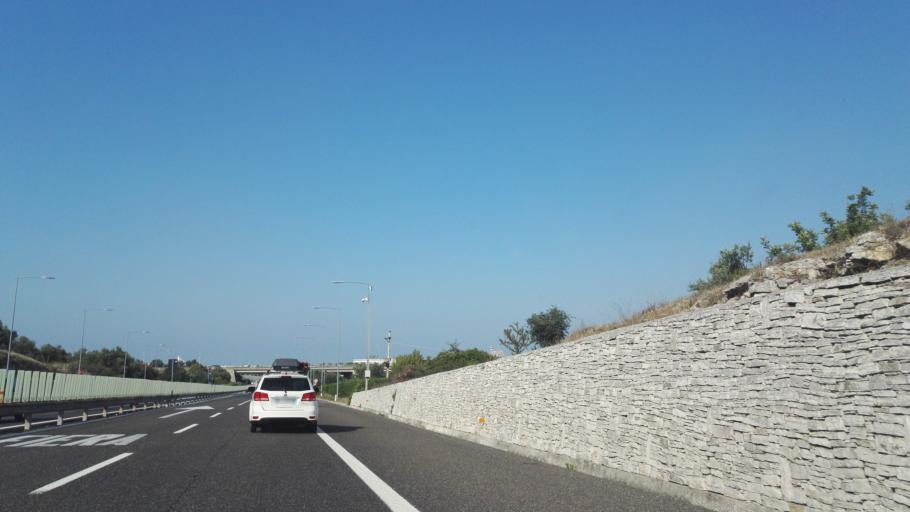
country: IT
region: Apulia
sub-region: Provincia di Bari
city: Modugno
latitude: 41.0961
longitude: 16.8217
